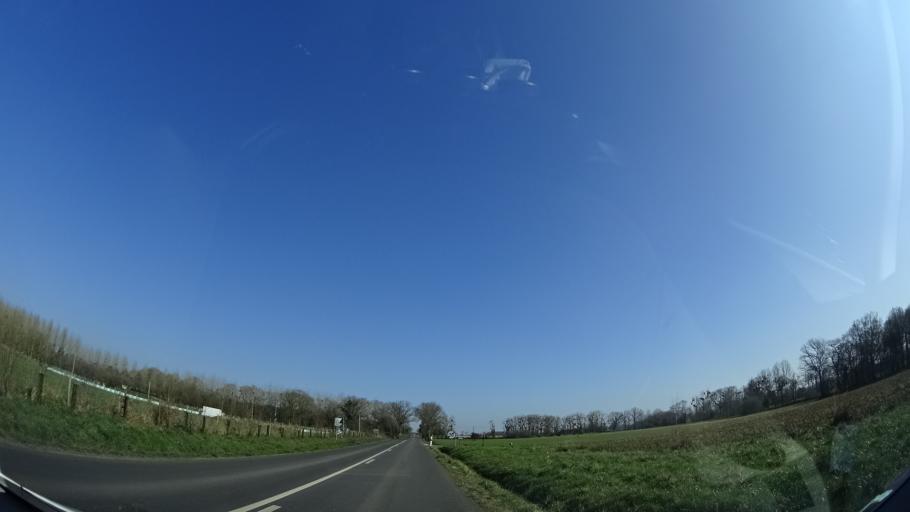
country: FR
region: Brittany
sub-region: Departement d'Ille-et-Vilaine
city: Meillac
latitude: 48.4107
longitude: -1.8040
